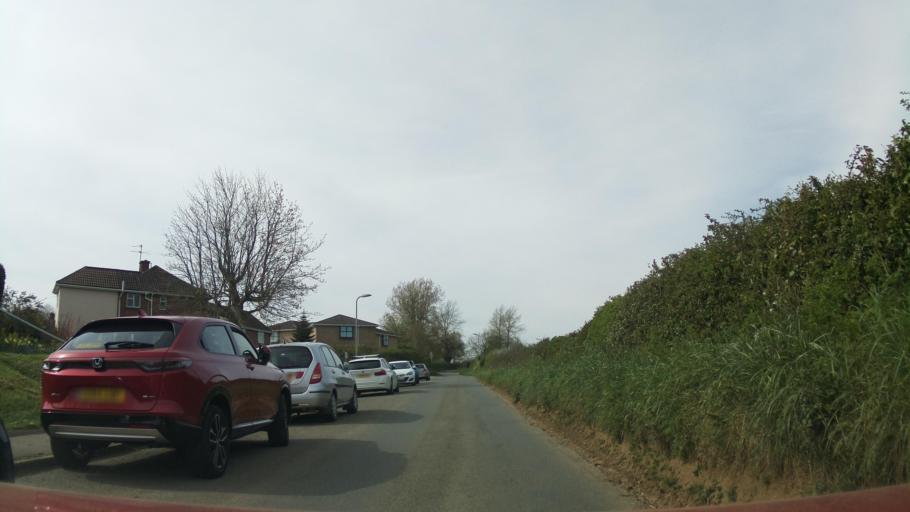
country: GB
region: England
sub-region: Dorset
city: Sherborne
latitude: 50.9583
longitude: -2.5111
